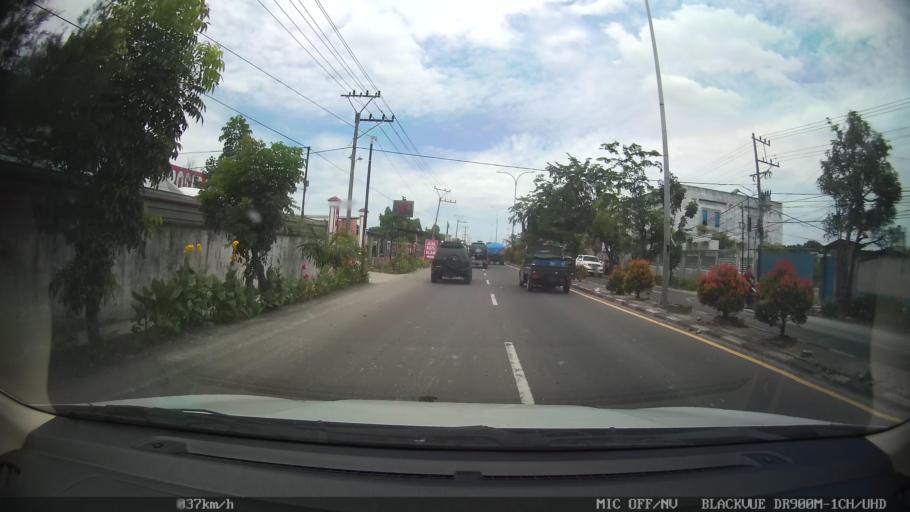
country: ID
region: North Sumatra
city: Sunggal
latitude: 3.5995
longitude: 98.5883
